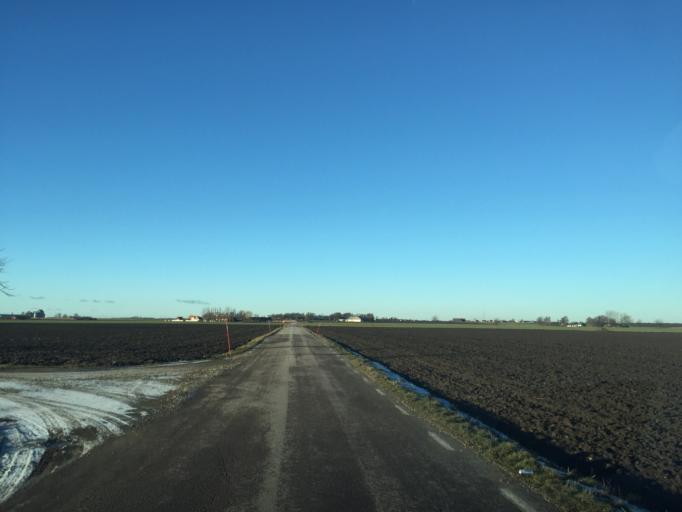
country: SE
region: Skane
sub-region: Kavlinge Kommun
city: Kaevlinge
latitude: 55.7468
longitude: 13.0888
